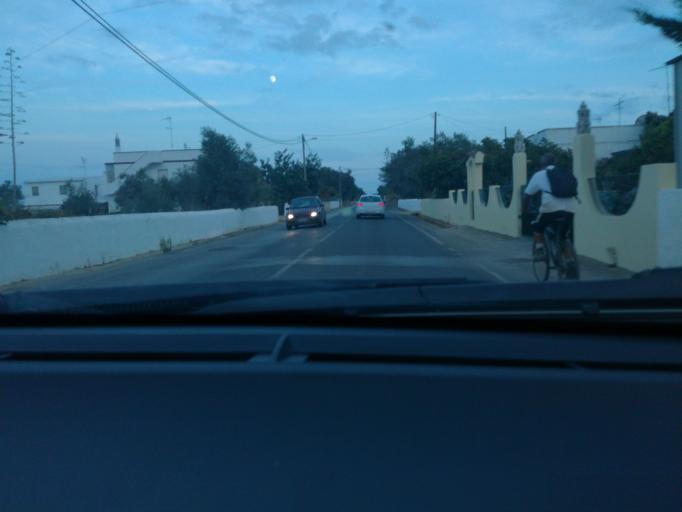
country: PT
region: Faro
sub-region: Olhao
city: Laranjeiro
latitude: 37.0626
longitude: -7.7583
